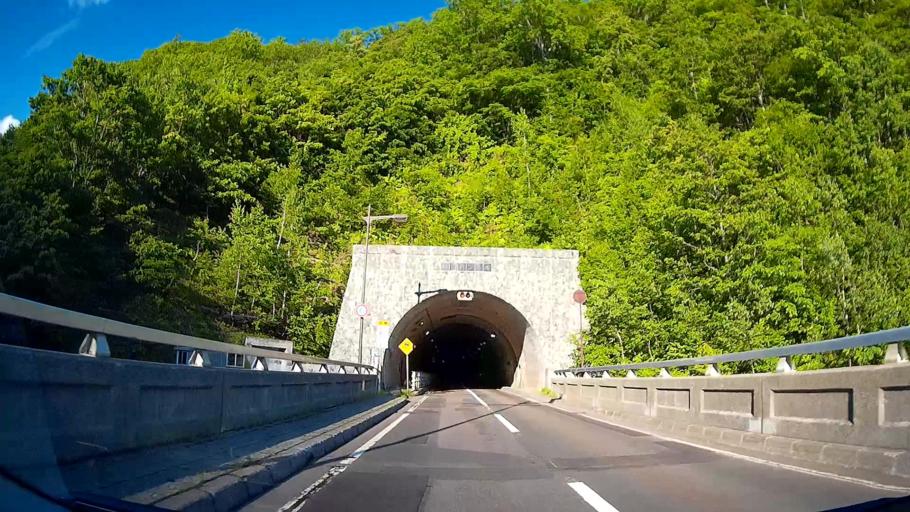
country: JP
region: Hokkaido
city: Sapporo
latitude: 42.9849
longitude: 141.1594
